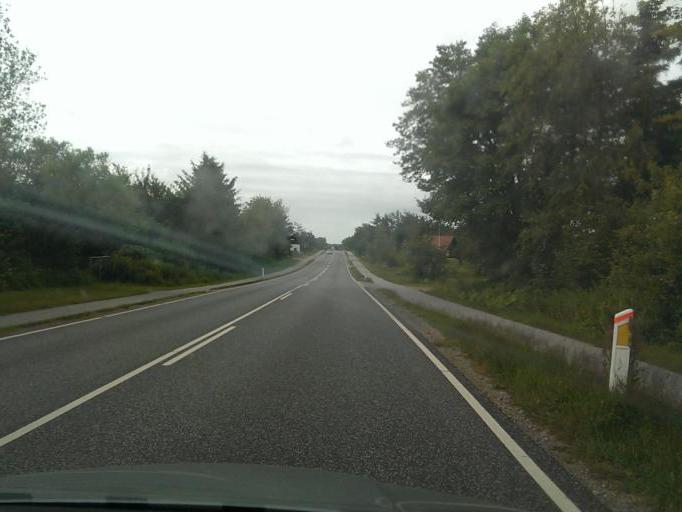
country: DK
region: North Denmark
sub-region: Hjorring Kommune
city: Hjorring
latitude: 57.4586
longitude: 9.9308
